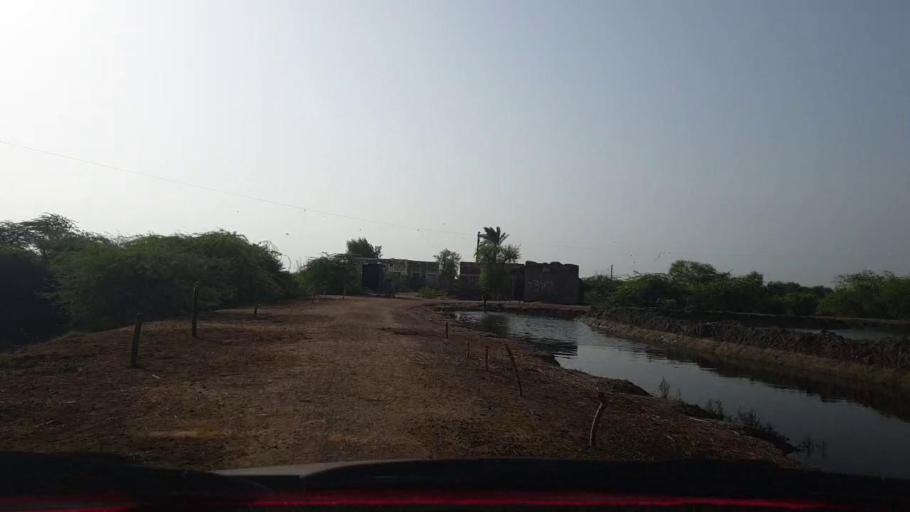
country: PK
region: Sindh
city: Talhar
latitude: 24.9249
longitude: 68.7512
